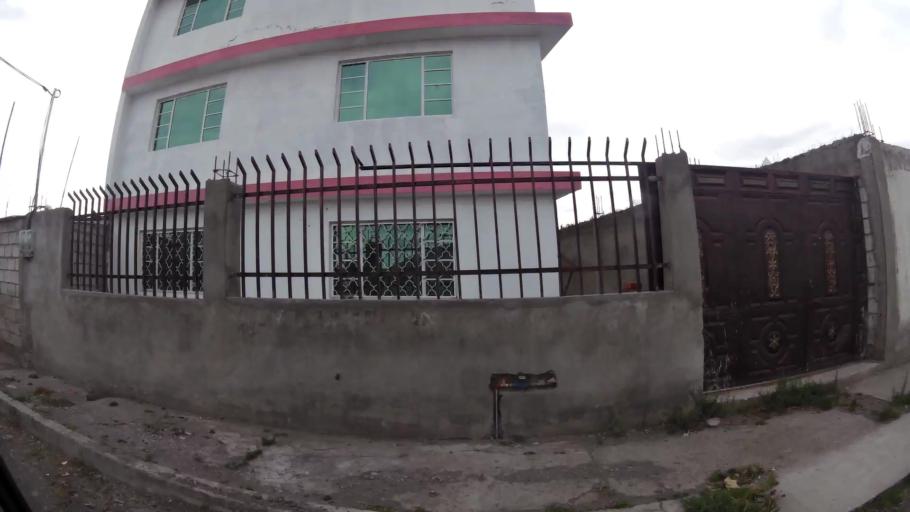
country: EC
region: Cotopaxi
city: Latacunga
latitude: -0.9515
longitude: -78.6174
